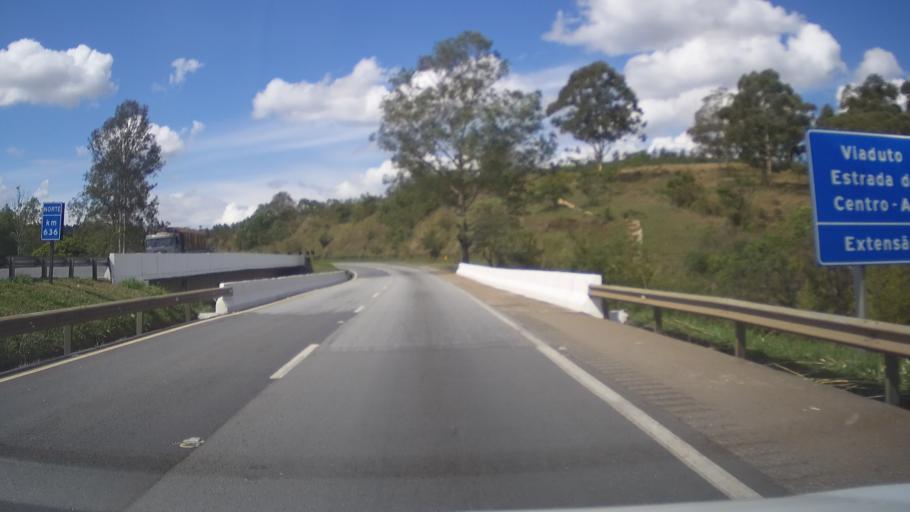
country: BR
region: Minas Gerais
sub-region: Santo Antonio Do Amparo
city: Santo Antonio do Amparo
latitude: -20.8669
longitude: -44.8416
